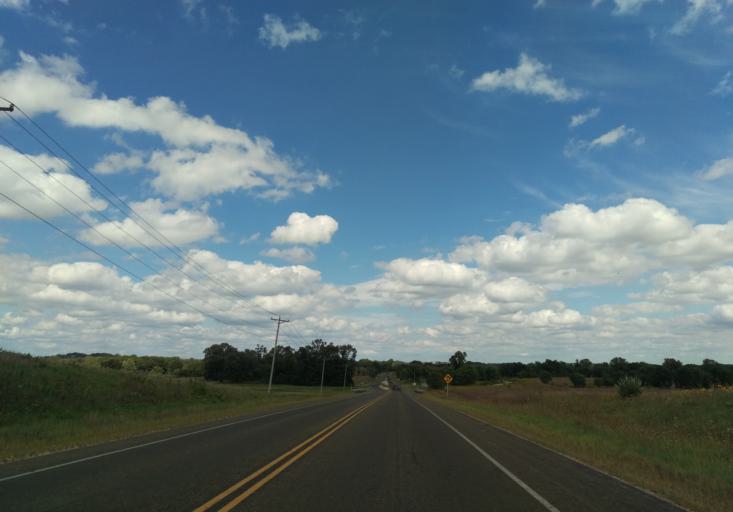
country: US
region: Wisconsin
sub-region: Dane County
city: Shorewood Hills
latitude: 43.1341
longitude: -89.4420
